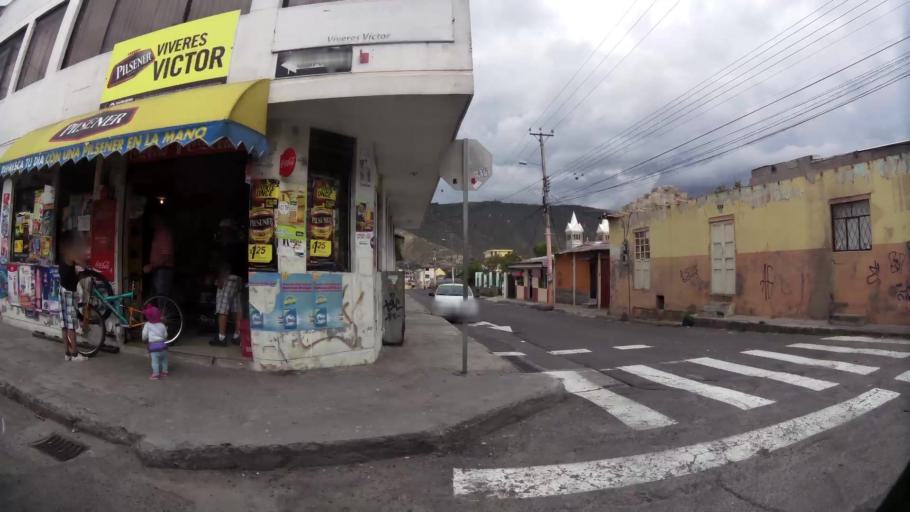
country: EC
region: Pichincha
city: Quito
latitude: -0.0128
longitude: -78.4485
